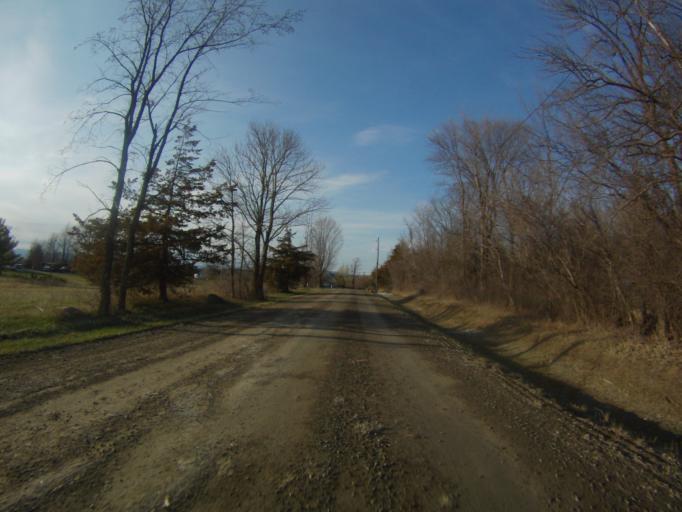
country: US
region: Vermont
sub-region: Addison County
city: Vergennes
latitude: 44.0710
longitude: -73.2935
